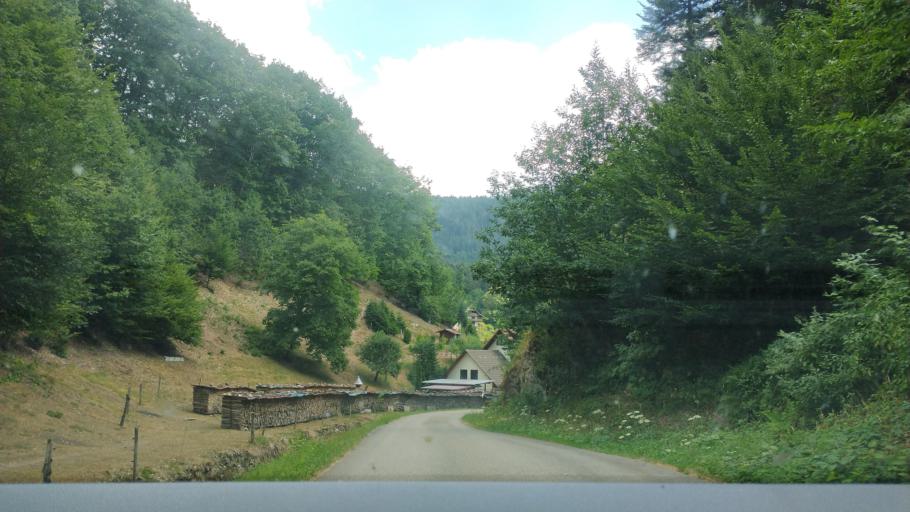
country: DE
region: Baden-Wuerttemberg
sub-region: Freiburg Region
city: Nordrach
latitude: 48.4250
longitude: 8.1142
